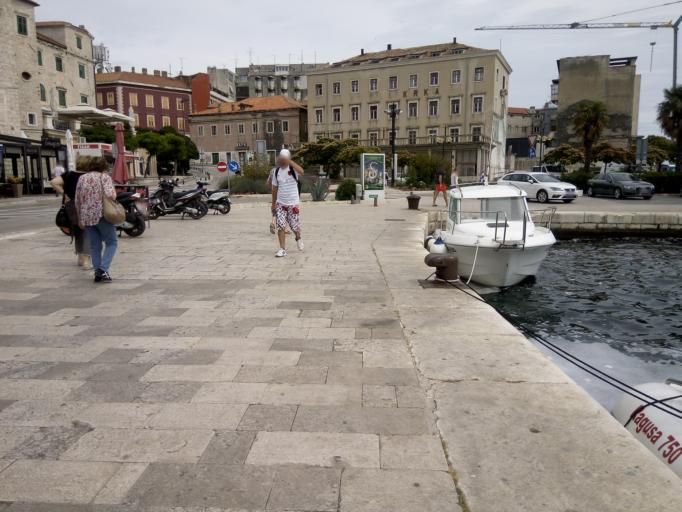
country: HR
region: Sibensko-Kniniska
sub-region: Grad Sibenik
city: Sibenik
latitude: 43.7337
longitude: 15.8912
